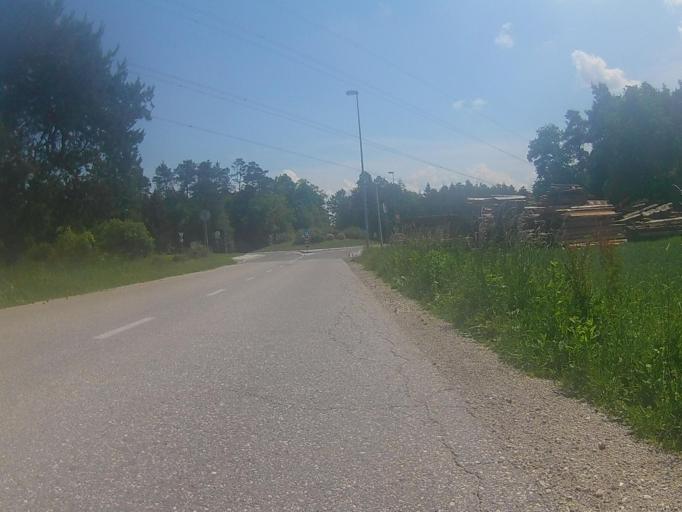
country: SI
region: Starse
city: Starse
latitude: 46.4392
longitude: 15.7732
